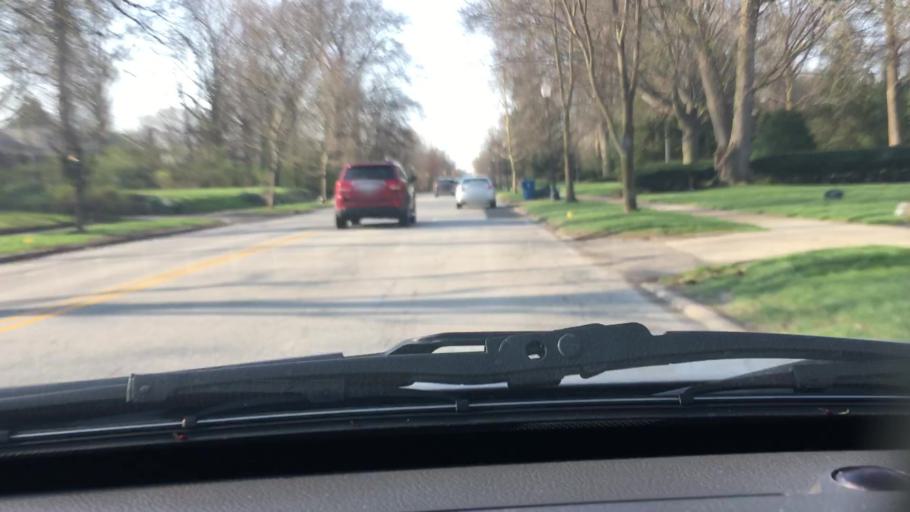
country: US
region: Indiana
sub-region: Marion County
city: Broad Ripple
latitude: 39.8420
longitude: -86.1571
